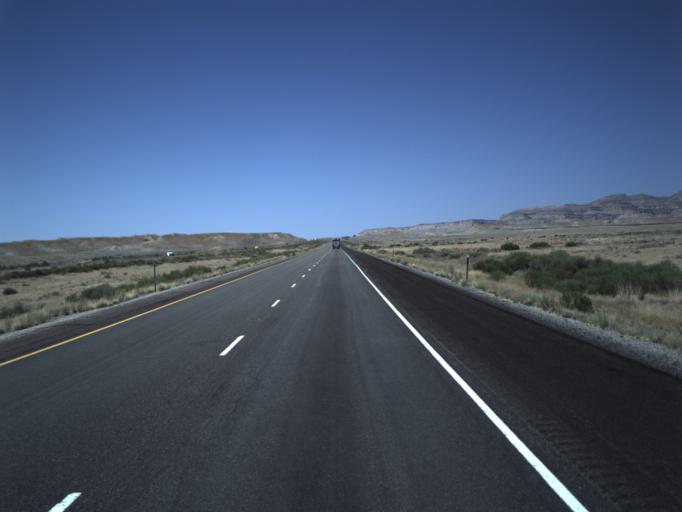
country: US
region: Utah
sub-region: Grand County
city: Moab
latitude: 38.9449
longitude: -109.6458
